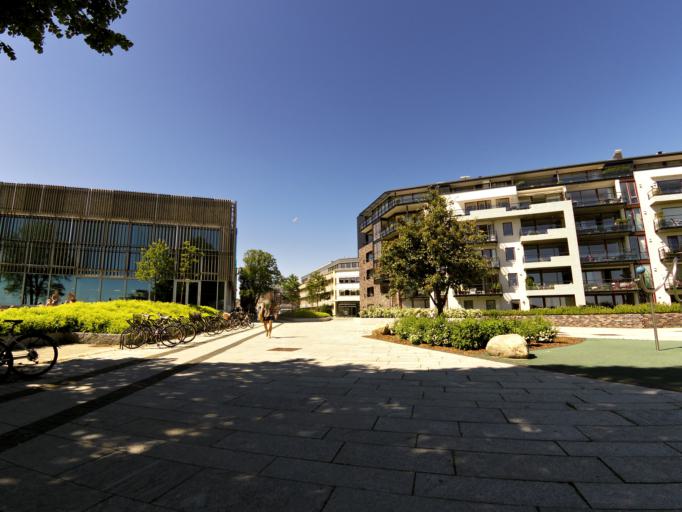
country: NO
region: Vest-Agder
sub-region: Kristiansand
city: Kristiansand
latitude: 58.1465
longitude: 8.0081
